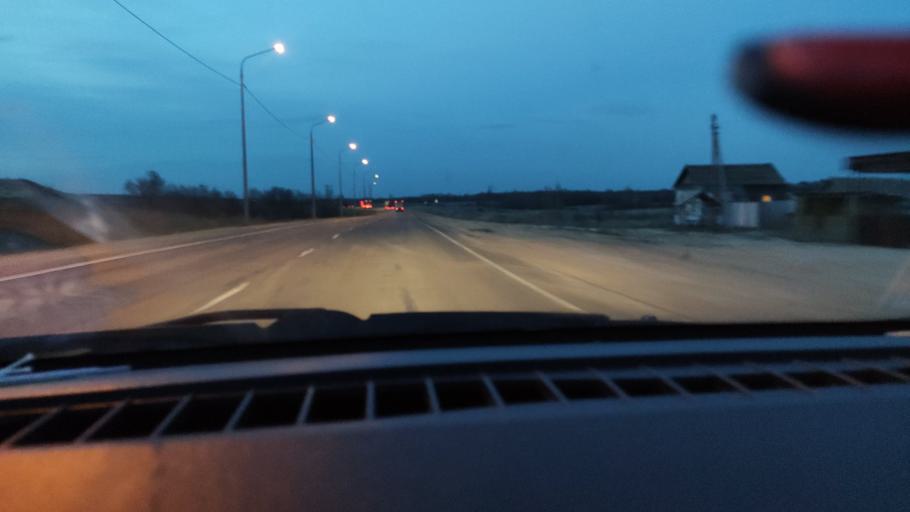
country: RU
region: Saratov
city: Sennoy
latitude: 52.0908
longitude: 46.8101
